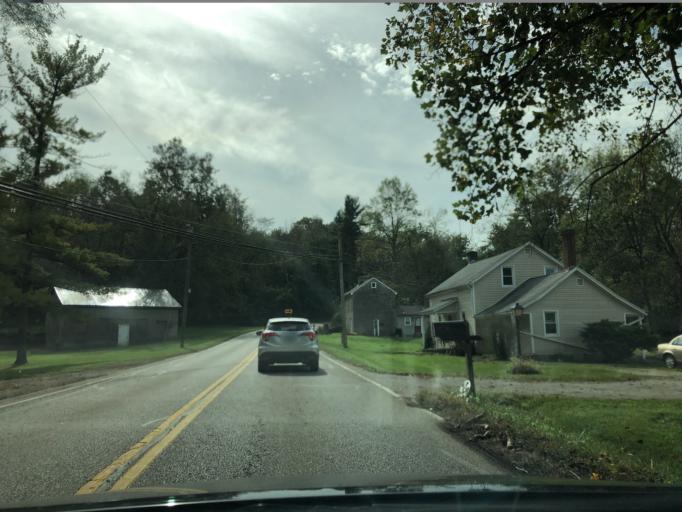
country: US
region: Ohio
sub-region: Clermont County
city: Milford
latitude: 39.1917
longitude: -84.2900
